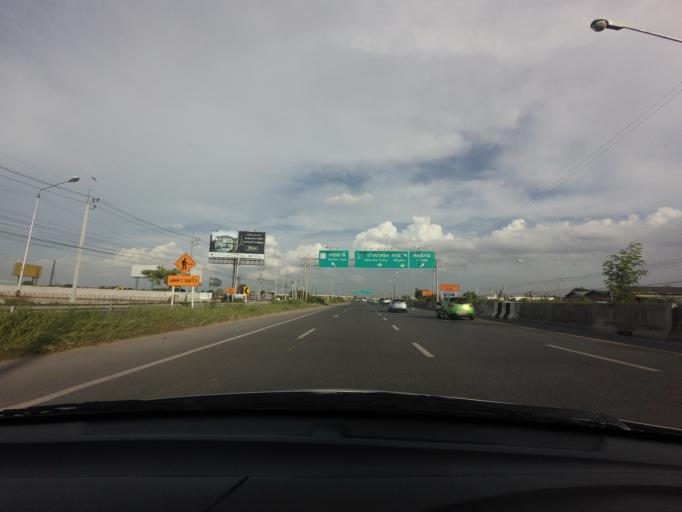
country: TH
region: Nonthaburi
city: Bang Bua Thong
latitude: 13.9450
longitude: 100.4147
